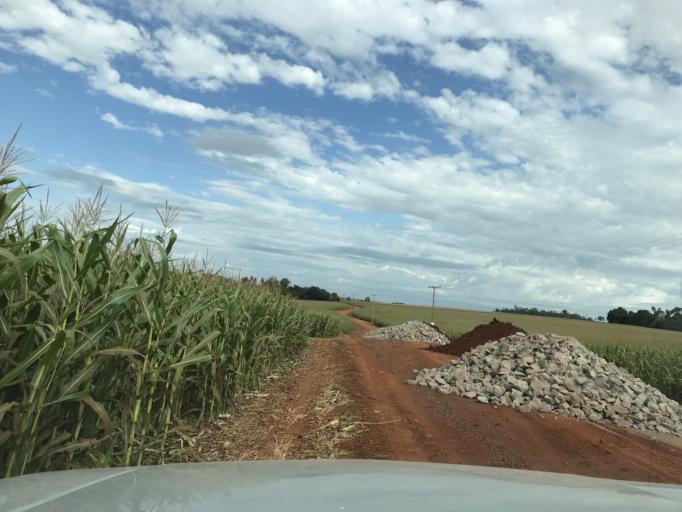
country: BR
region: Parana
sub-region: Palotina
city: Palotina
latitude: -24.3054
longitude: -53.8088
